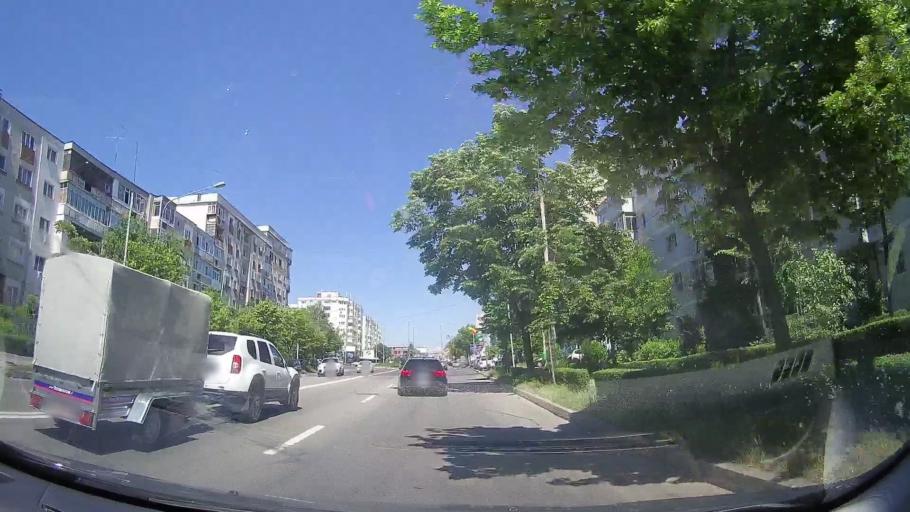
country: RO
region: Arges
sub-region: Comuna Bradu
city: Geamana
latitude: 44.8380
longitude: 24.9000
